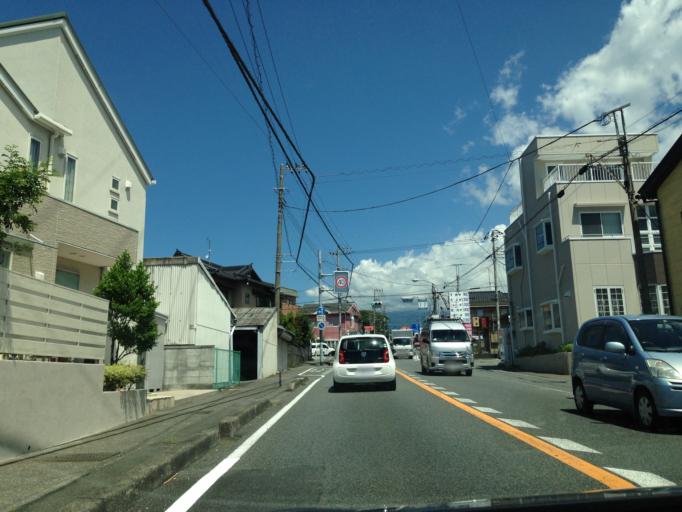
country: JP
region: Shizuoka
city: Fuji
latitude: 35.1669
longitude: 138.6890
